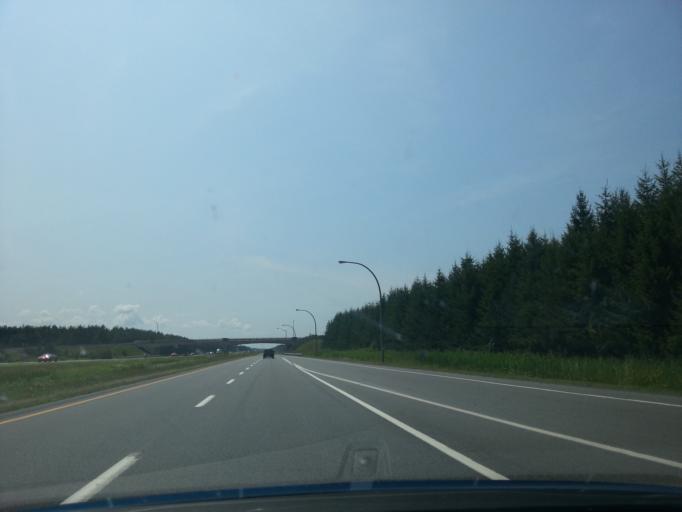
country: CA
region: Quebec
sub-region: Mauricie
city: Daveluyville
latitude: 46.2675
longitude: -72.0191
